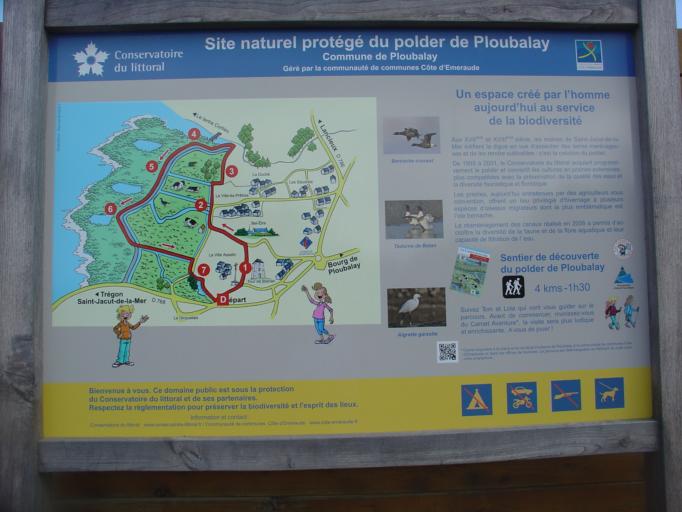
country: FR
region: Brittany
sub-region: Departement des Cotes-d'Armor
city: Ploubalay
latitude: 48.5762
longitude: -2.1553
